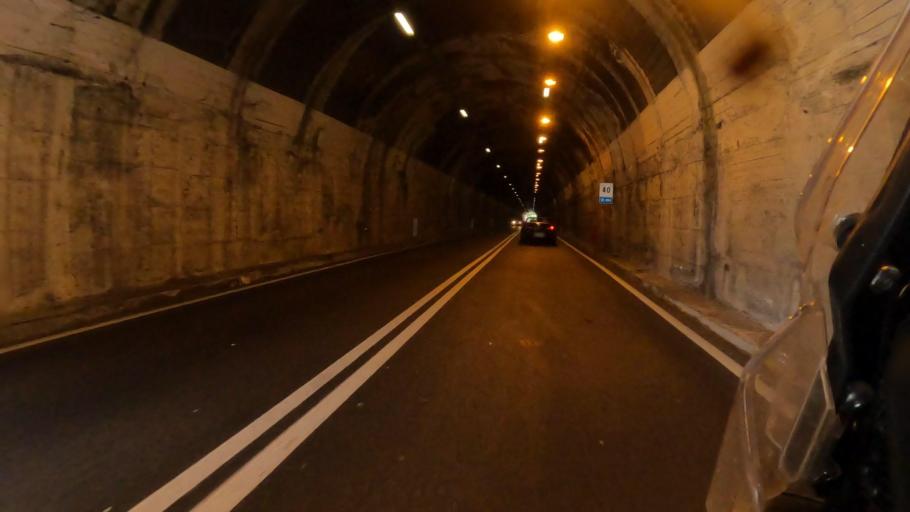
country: IT
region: Lombardy
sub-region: Provincia di Varese
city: Maccagno
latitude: 46.0337
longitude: 8.7462
